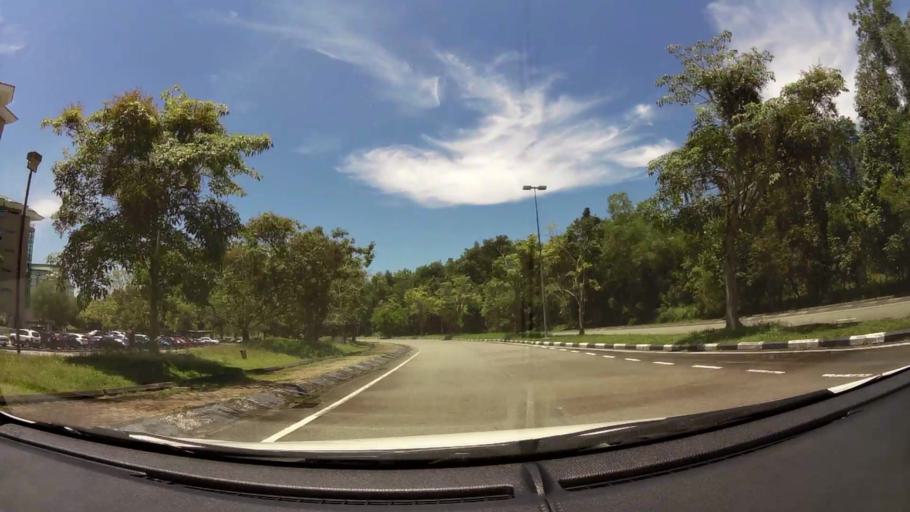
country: BN
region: Brunei and Muara
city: Bandar Seri Begawan
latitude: 4.9166
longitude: 114.9434
